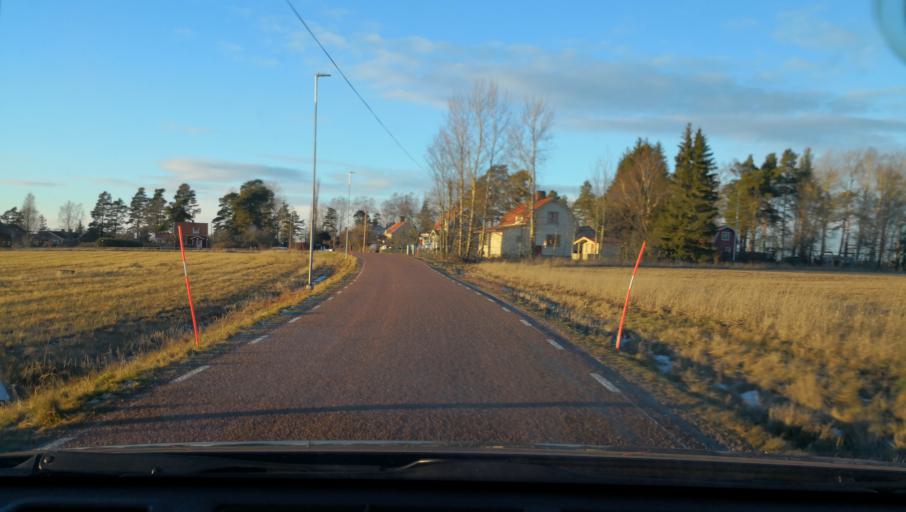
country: SE
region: Vaestmanland
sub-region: Vasteras
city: Tillberga
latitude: 59.6916
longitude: 16.6069
